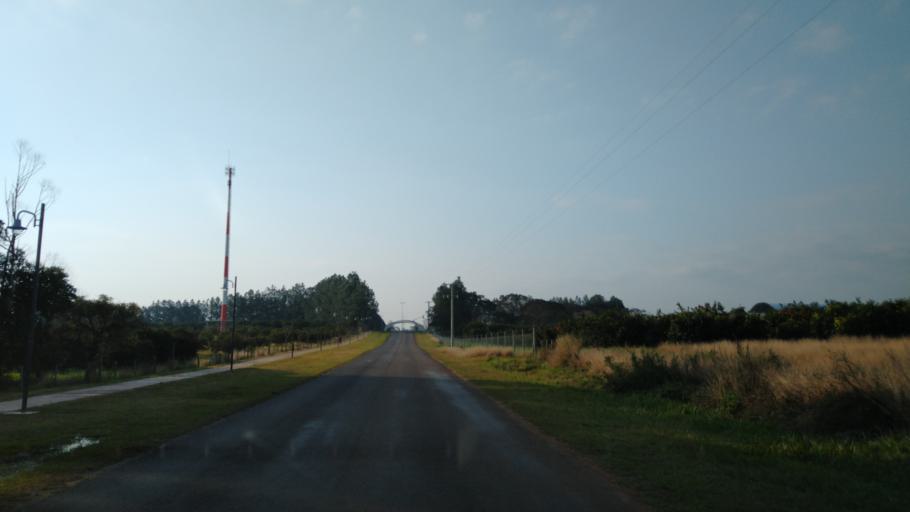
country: AR
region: Entre Rios
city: Santa Ana
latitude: -30.9027
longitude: -57.9247
